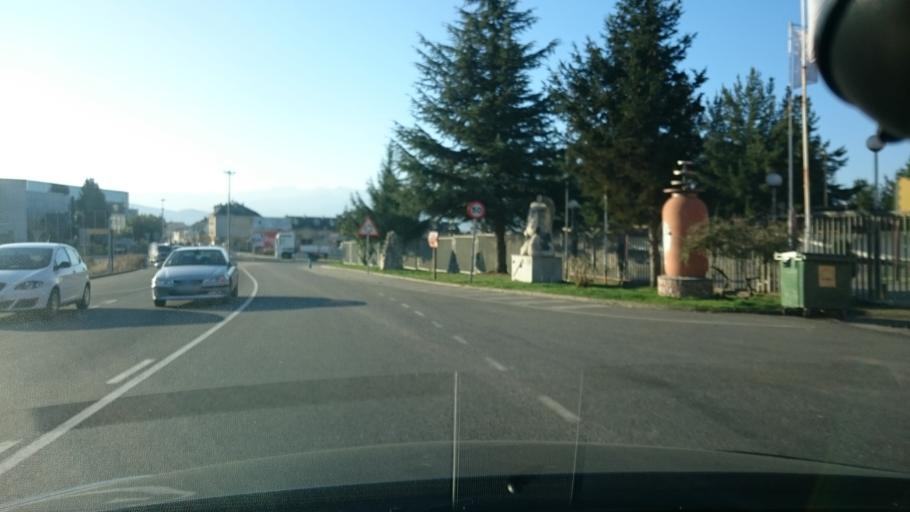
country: ES
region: Castille and Leon
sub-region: Provincia de Leon
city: Camponaraya
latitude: 42.5842
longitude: -6.6753
